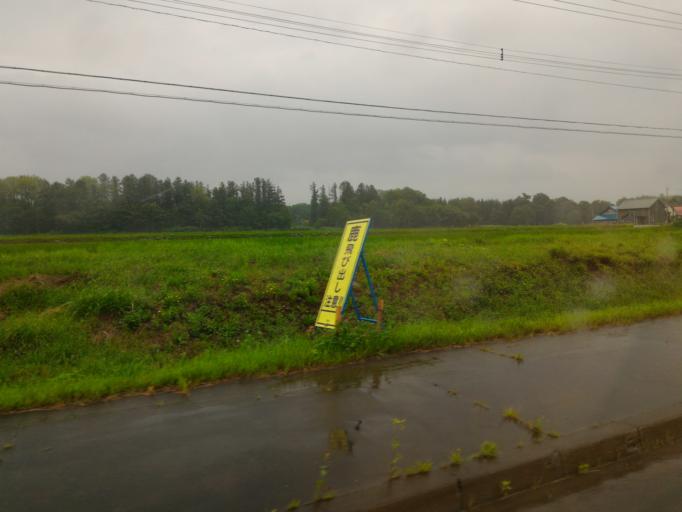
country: JP
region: Hokkaido
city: Nayoro
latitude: 44.5088
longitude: 142.3335
